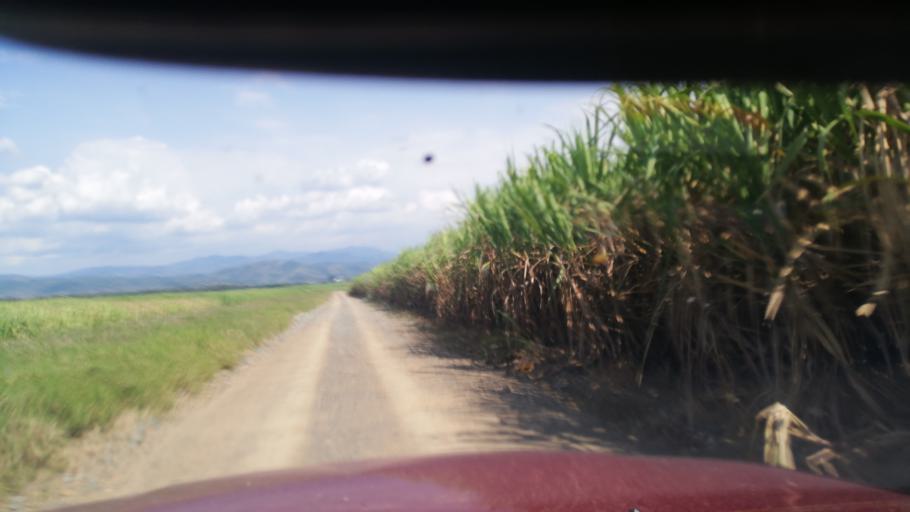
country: CO
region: Risaralda
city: La Virginia
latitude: 4.8921
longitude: -75.9237
